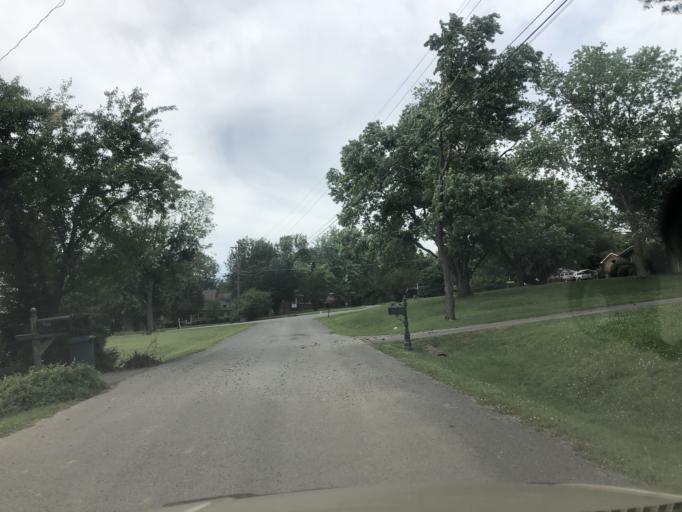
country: US
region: Tennessee
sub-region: Davidson County
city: Lakewood
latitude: 36.2600
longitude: -86.6131
